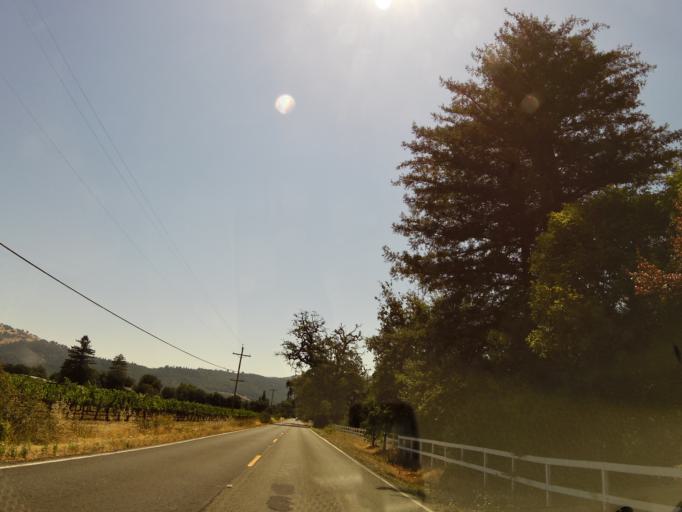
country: US
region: California
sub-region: Sonoma County
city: Cloverdale
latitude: 38.8242
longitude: -123.0306
